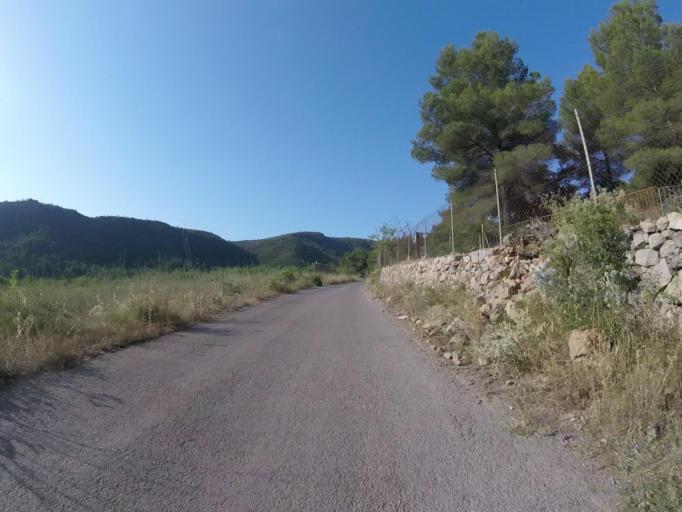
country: ES
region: Valencia
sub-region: Provincia de Castello
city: Benicassim
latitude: 40.1027
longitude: 0.0645
